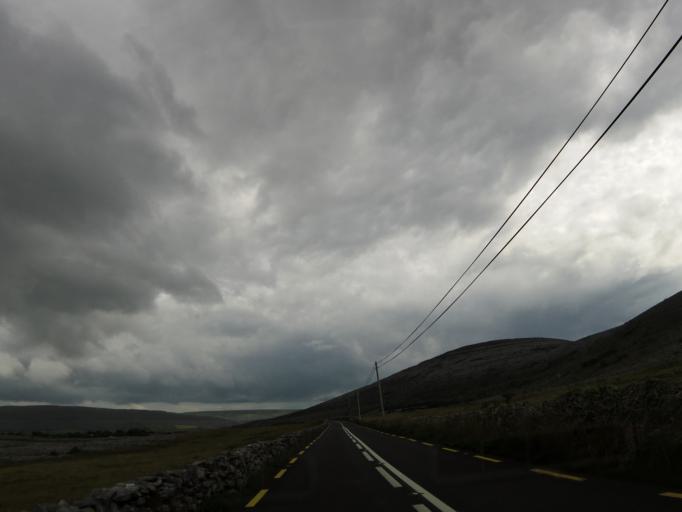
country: IE
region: Connaught
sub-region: County Galway
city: Bearna
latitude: 53.1351
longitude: -9.0989
